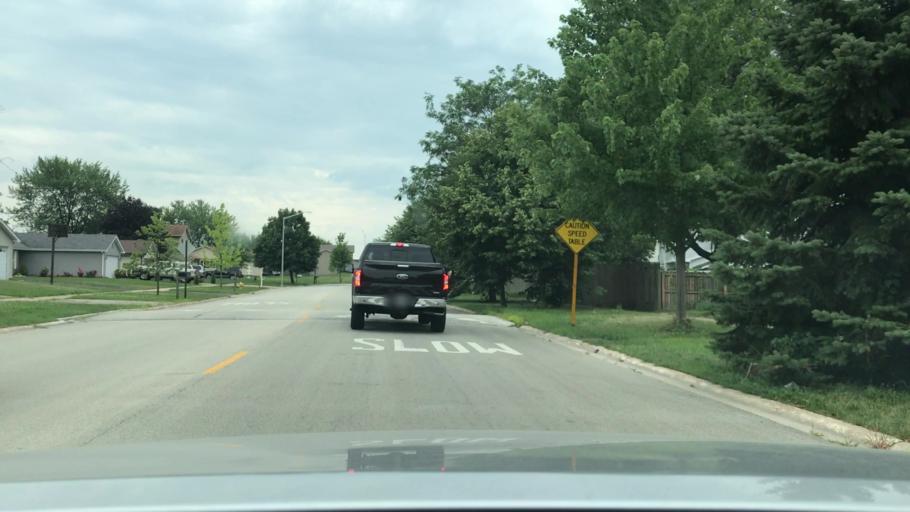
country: US
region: Illinois
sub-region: Will County
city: Bolingbrook
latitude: 41.7040
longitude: -88.0389
